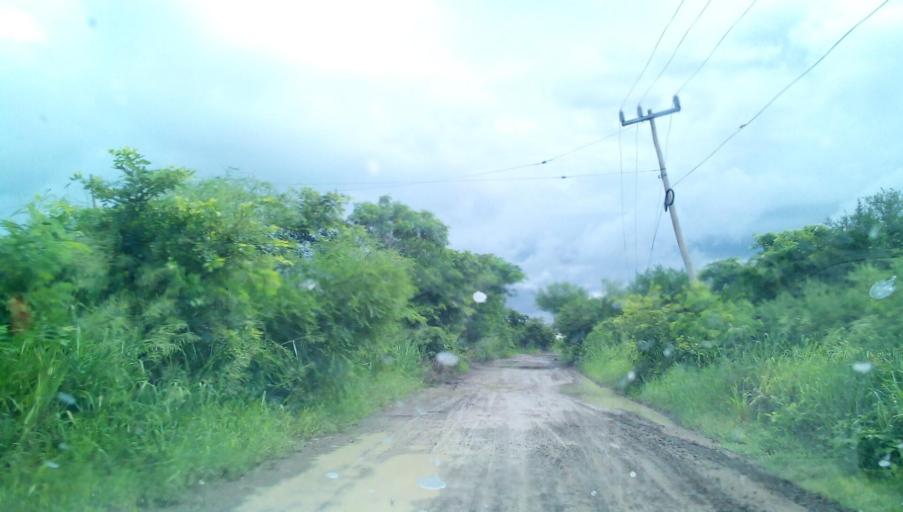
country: MX
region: Veracruz
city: Panuco
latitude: 21.8437
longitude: -98.1344
